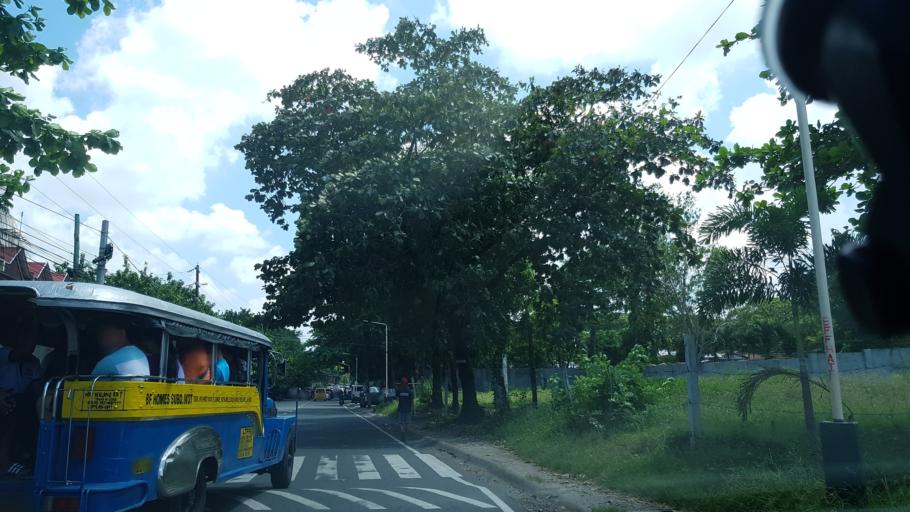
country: PH
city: Sambayanihan People's Village
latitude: 14.4503
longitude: 121.0053
